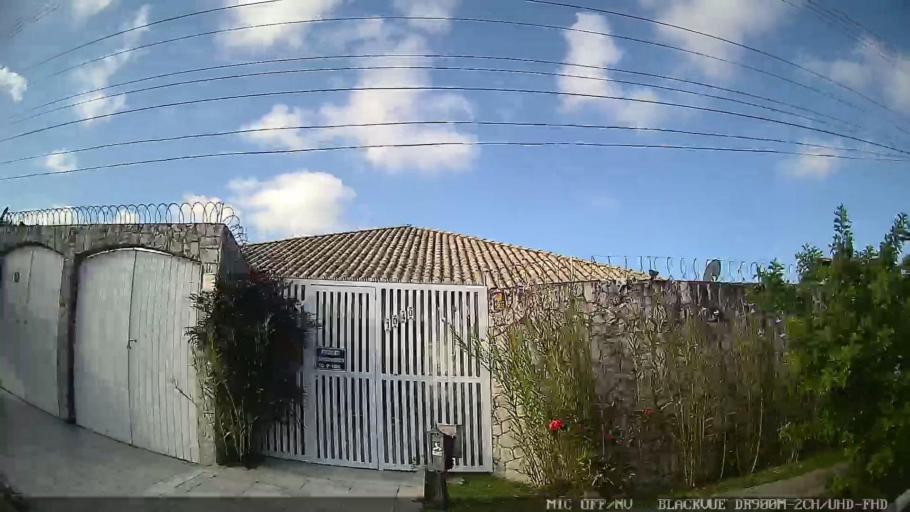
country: BR
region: Sao Paulo
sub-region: Peruibe
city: Peruibe
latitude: -24.2880
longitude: -46.9686
